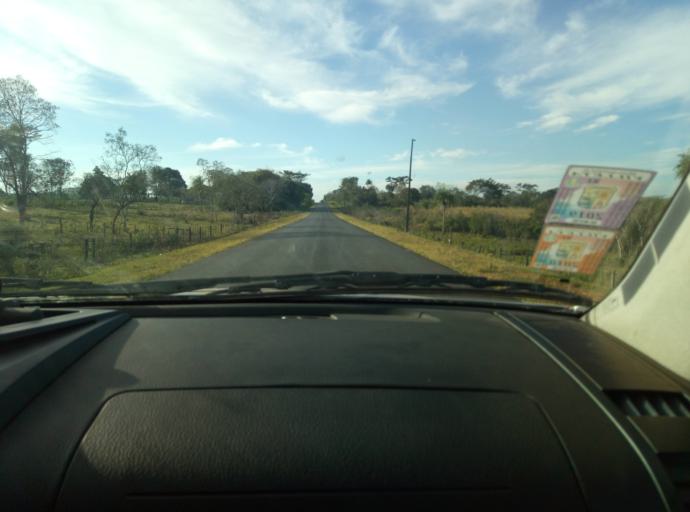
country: PY
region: Caaguazu
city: Carayao
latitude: -25.1649
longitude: -56.3126
